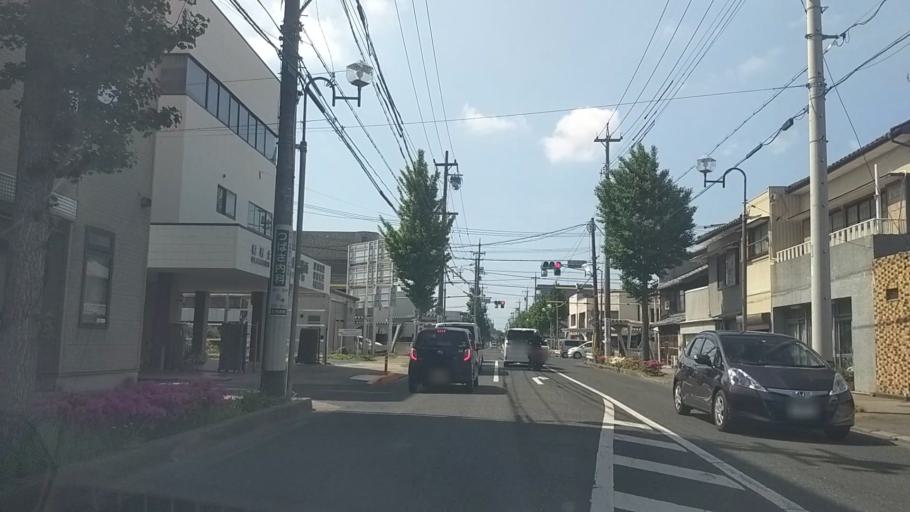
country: JP
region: Shizuoka
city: Hamamatsu
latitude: 34.7041
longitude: 137.7421
